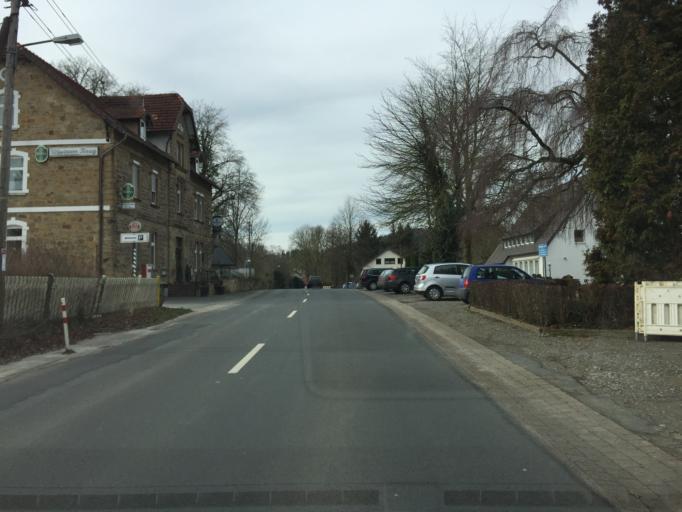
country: DE
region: North Rhine-Westphalia
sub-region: Regierungsbezirk Detmold
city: Bad Salzuflen
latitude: 52.1031
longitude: 8.7954
